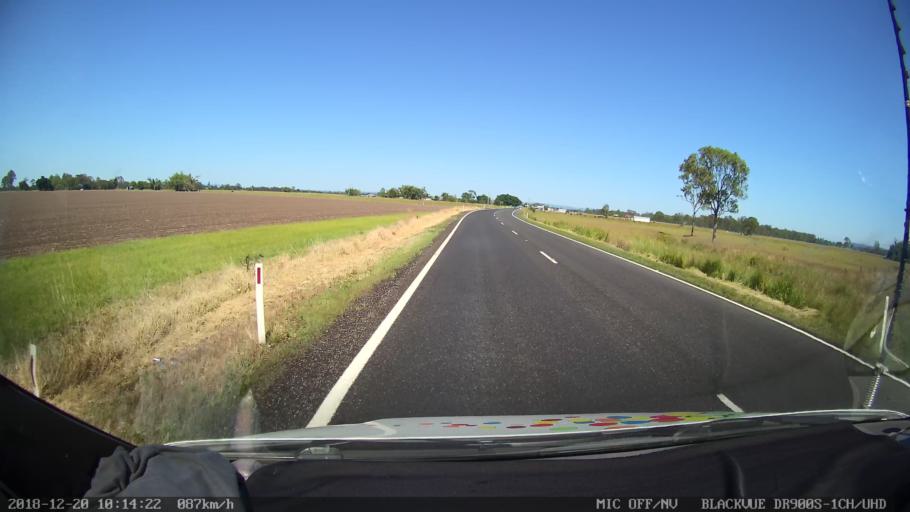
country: AU
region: New South Wales
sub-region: Richmond Valley
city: Casino
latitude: -28.8701
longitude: 153.1159
